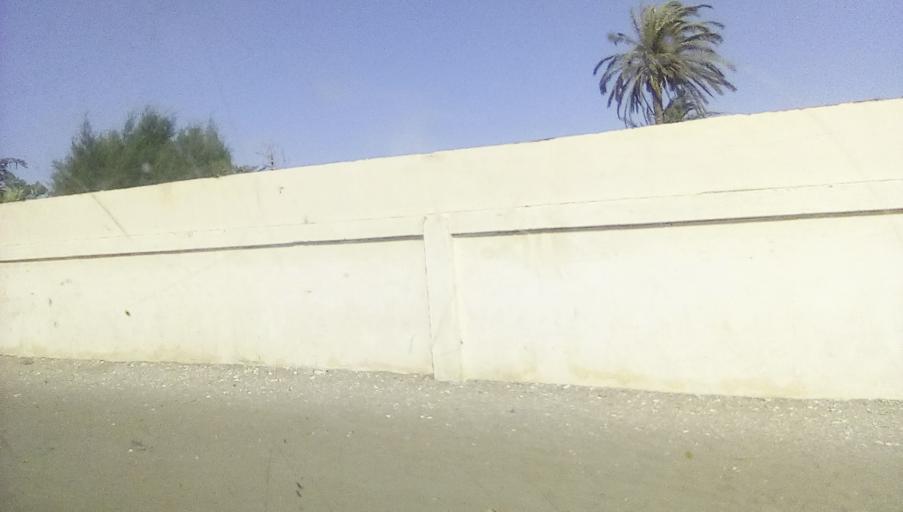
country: SN
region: Saint-Louis
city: Saint-Louis
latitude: 16.0278
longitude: -16.4755
